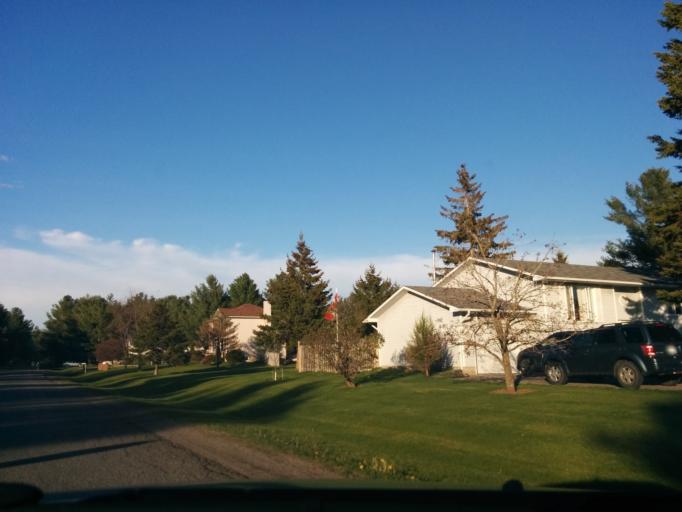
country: CA
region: Ontario
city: Ottawa
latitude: 45.1489
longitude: -75.5985
